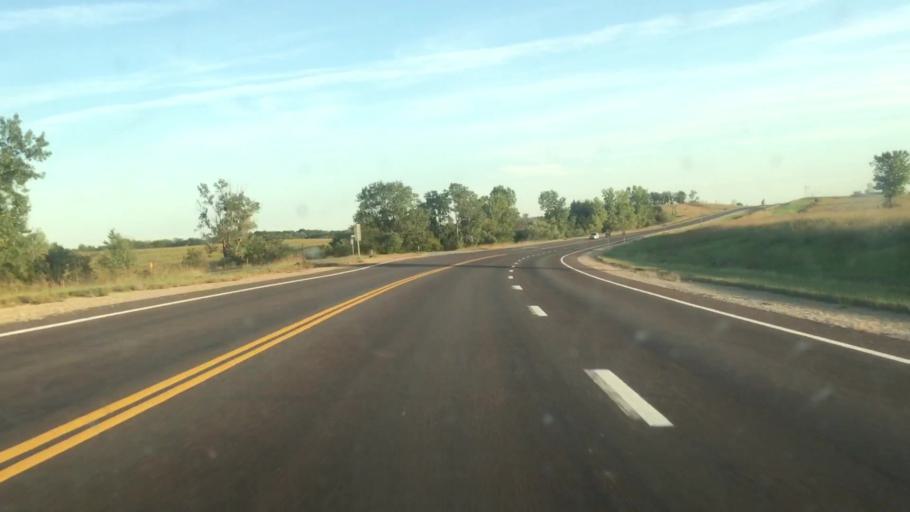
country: US
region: Kansas
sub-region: Atchison County
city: Atchison
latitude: 39.4685
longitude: -95.0954
